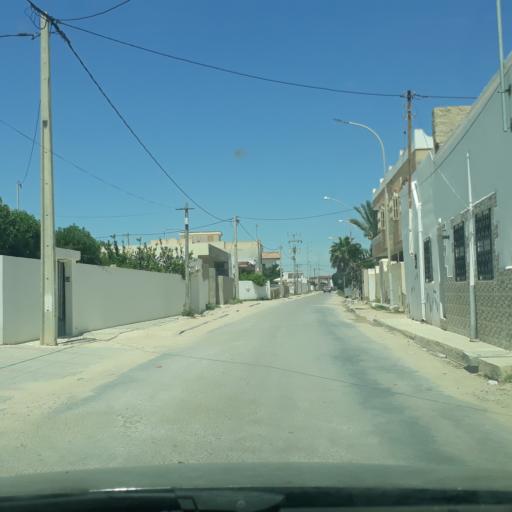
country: TN
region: Safaqis
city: Al Qarmadah
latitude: 34.8125
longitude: 10.7589
